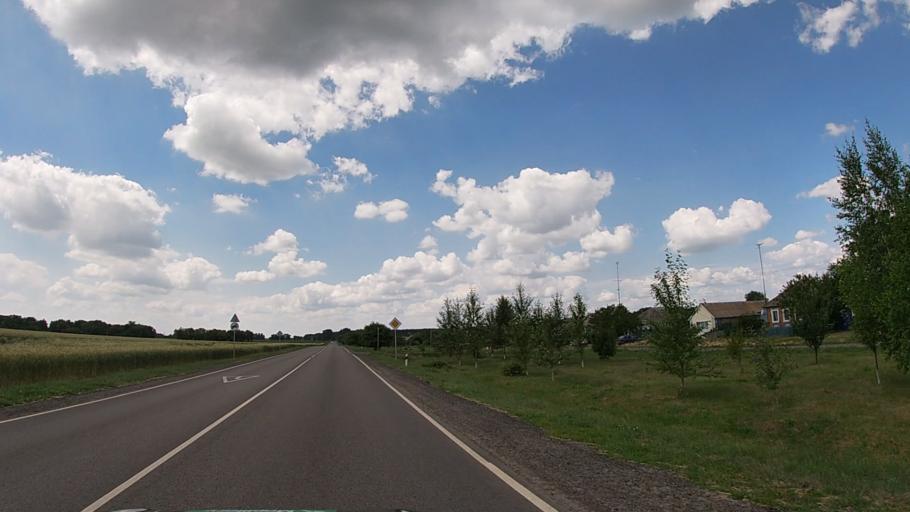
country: RU
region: Belgorod
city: Golovchino
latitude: 50.5120
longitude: 35.7616
